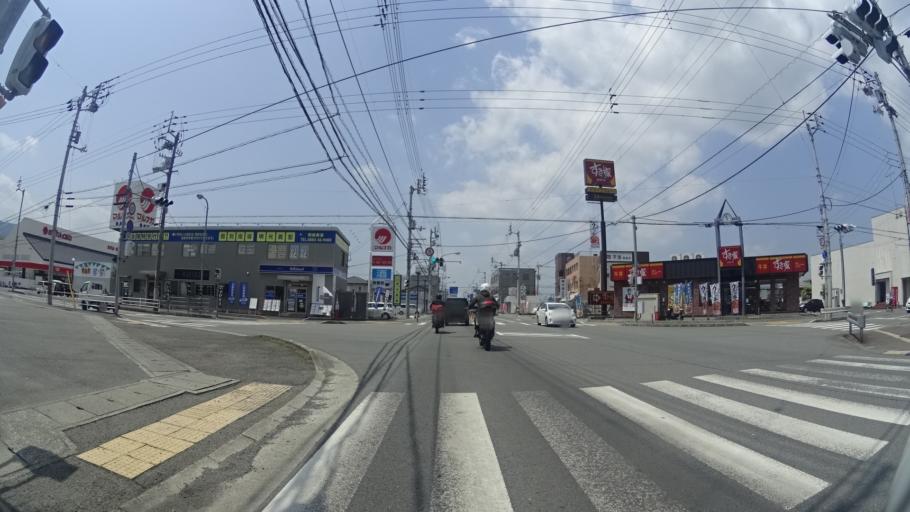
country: JP
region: Tokushima
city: Kamojimacho-jogejima
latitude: 34.0681
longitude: 134.3555
